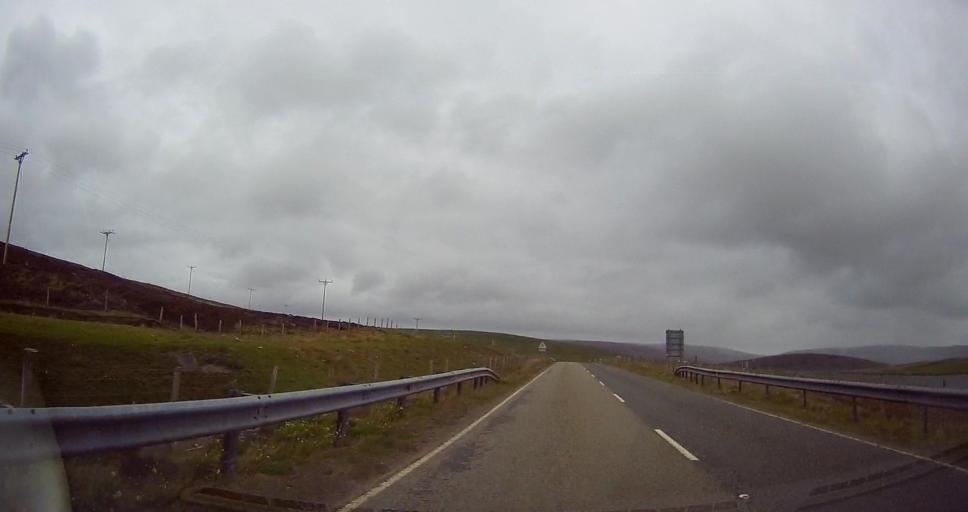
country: GB
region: Scotland
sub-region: Shetland Islands
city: Lerwick
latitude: 60.2566
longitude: -1.4336
